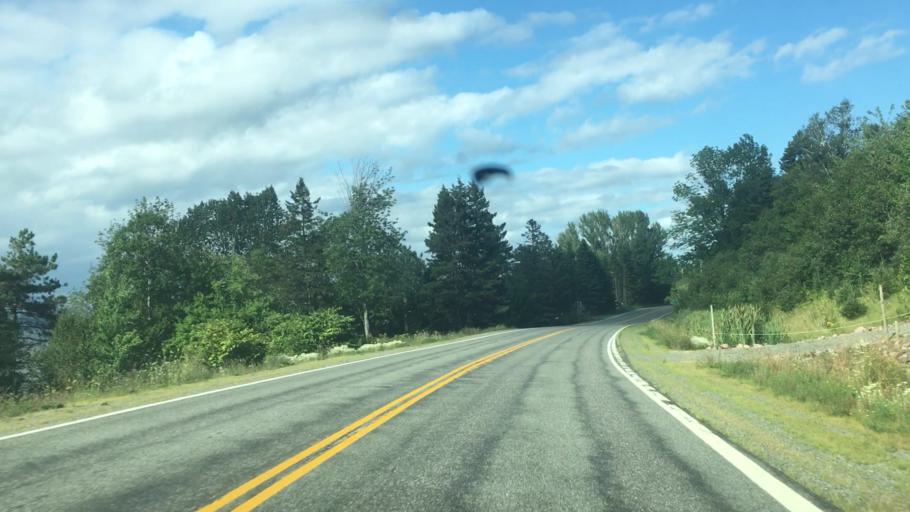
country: CA
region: Nova Scotia
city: Sydney
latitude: 45.8733
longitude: -60.6053
